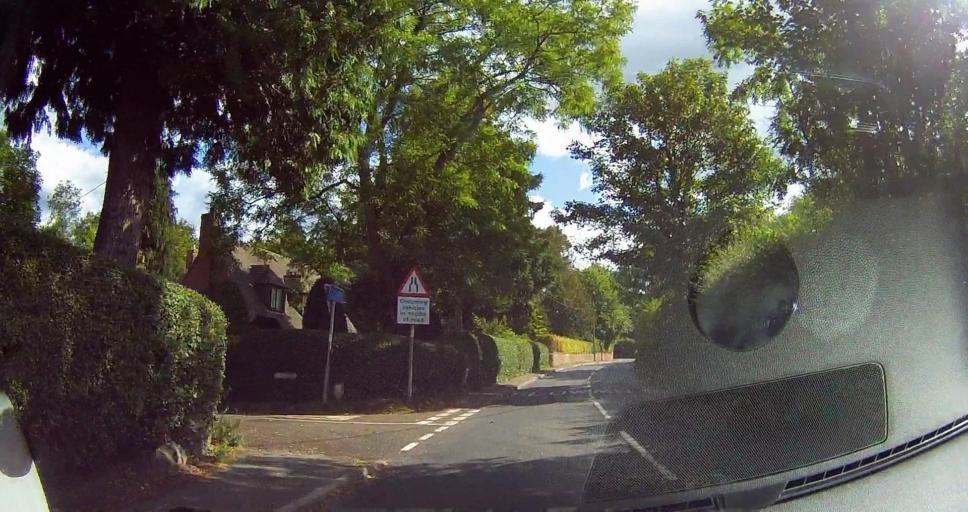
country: GB
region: England
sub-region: Cheshire East
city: Willaston
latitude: 52.9889
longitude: -2.5029
